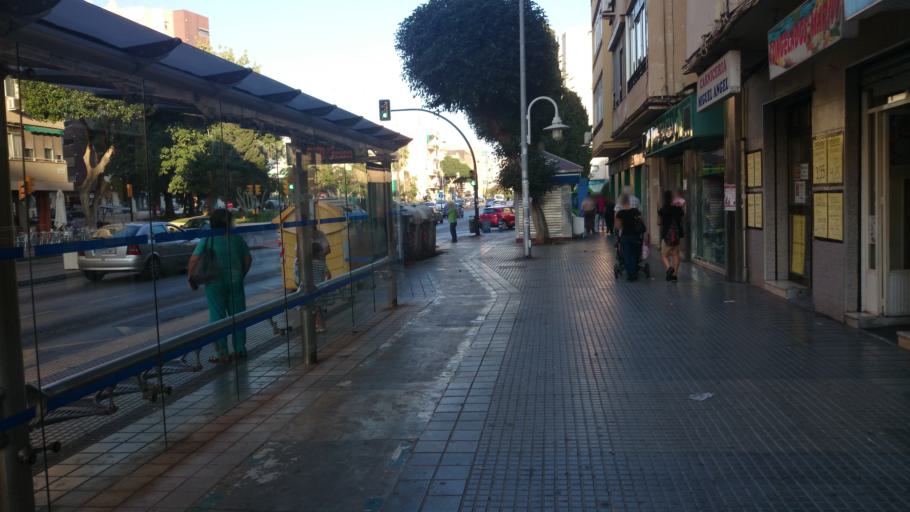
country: ES
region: Andalusia
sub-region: Provincia de Malaga
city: Malaga
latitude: 36.7216
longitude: -4.4410
